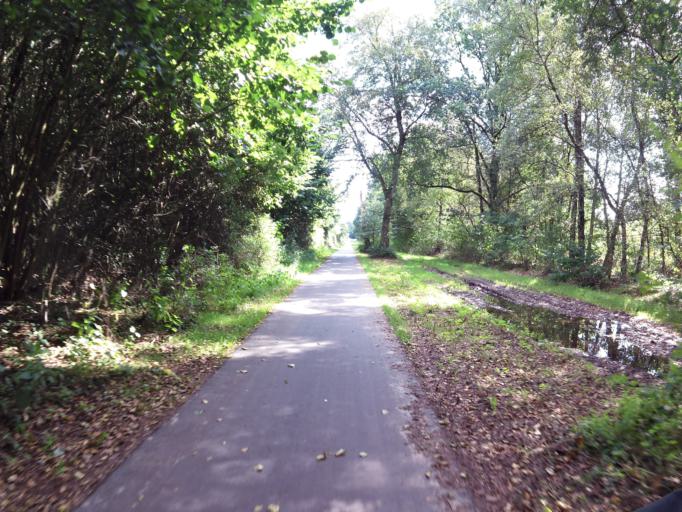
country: NL
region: Drenthe
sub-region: Gemeente Aa en Hunze
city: Anloo
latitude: 52.9904
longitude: 6.7098
